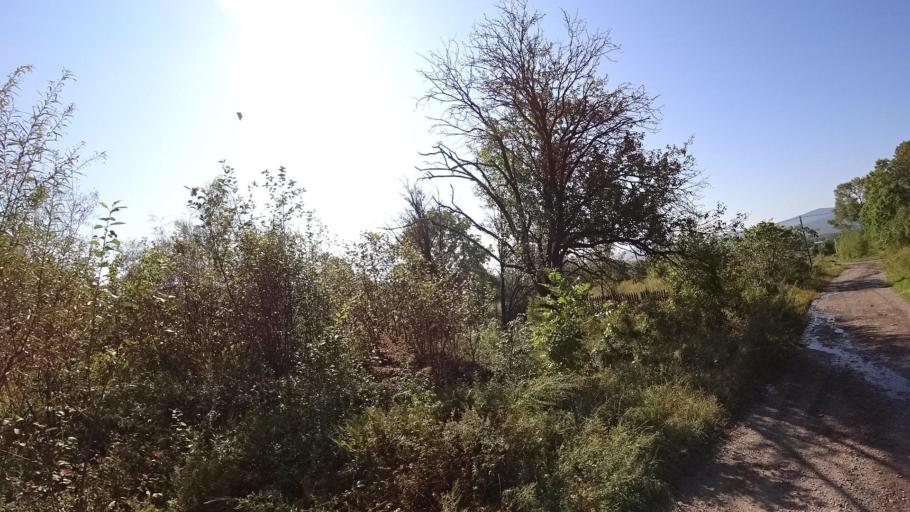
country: RU
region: Jewish Autonomous Oblast
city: Bira
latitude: 49.0013
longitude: 132.4719
